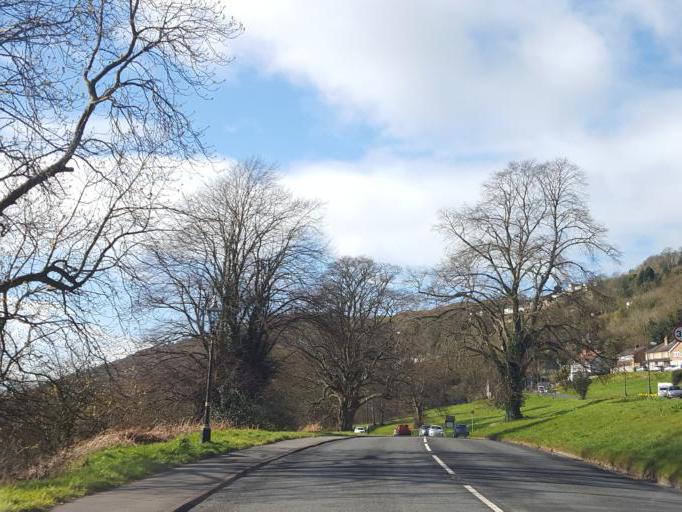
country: GB
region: England
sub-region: Worcestershire
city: Great Malvern
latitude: 52.0971
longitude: -2.3315
